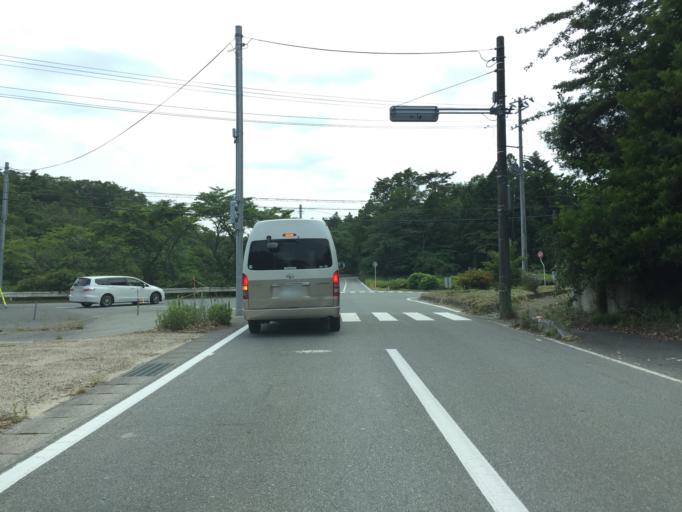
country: JP
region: Fukushima
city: Namie
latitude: 37.3148
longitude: 141.0075
